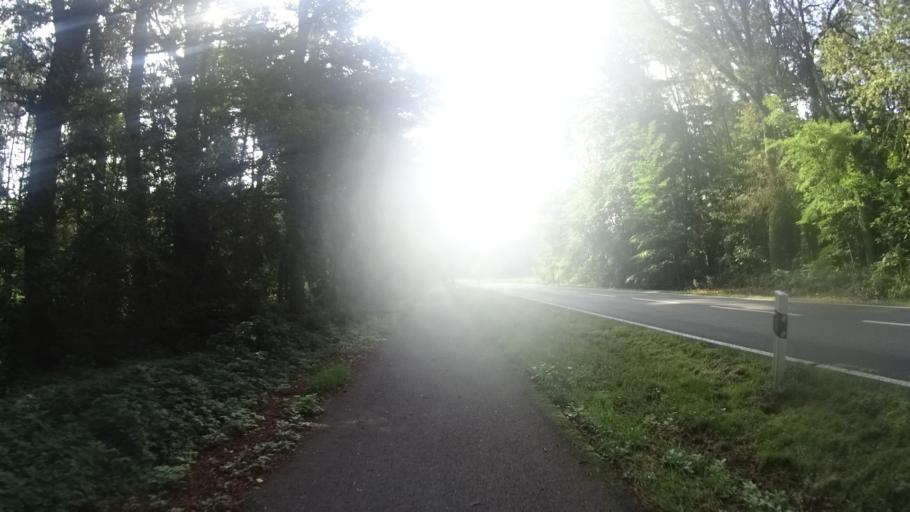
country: DE
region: Brandenburg
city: Cumlosen
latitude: 53.0182
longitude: 11.7021
